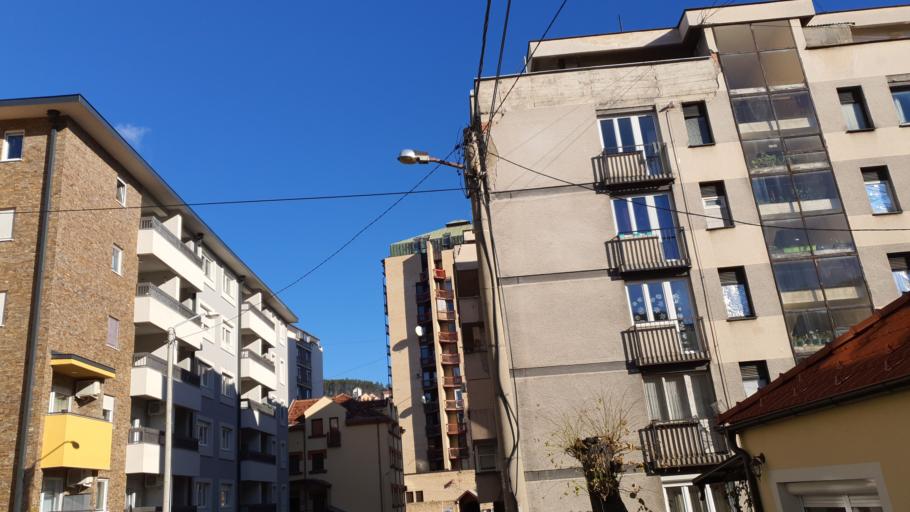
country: RS
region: Central Serbia
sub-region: Zlatiborski Okrug
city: Uzice
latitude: 43.8583
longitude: 19.8379
